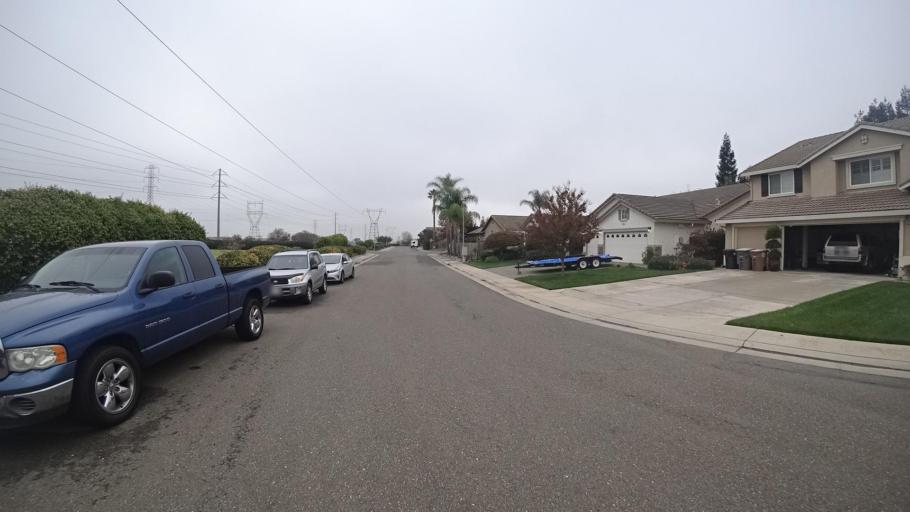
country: US
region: California
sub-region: Sacramento County
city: Elk Grove
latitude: 38.4034
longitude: -121.3512
